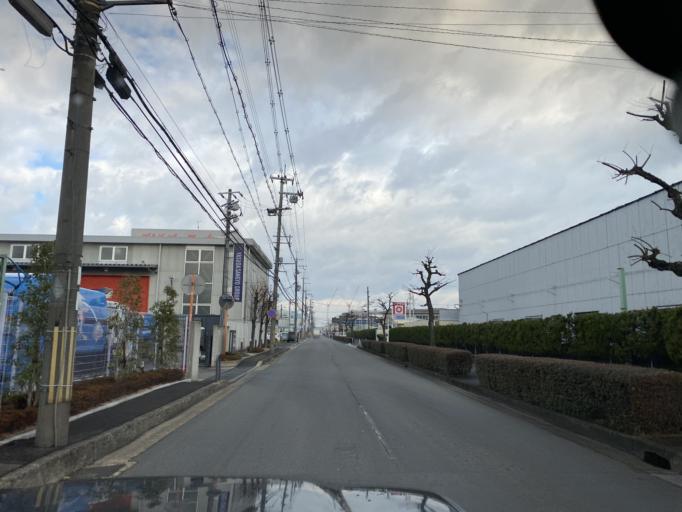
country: JP
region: Kyoto
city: Yawata
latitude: 34.8771
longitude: 135.7453
